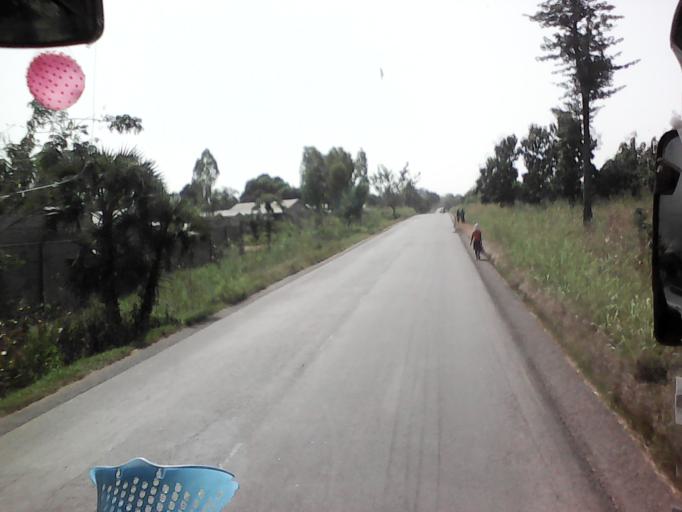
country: TG
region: Centrale
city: Sokode
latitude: 8.8393
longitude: 1.0739
